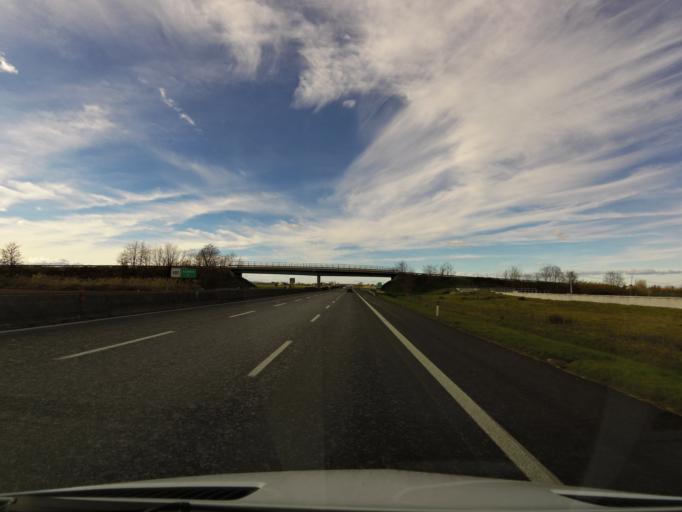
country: IT
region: Emilia-Romagna
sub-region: Forli-Cesena
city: Sala
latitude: 44.1354
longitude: 12.3634
